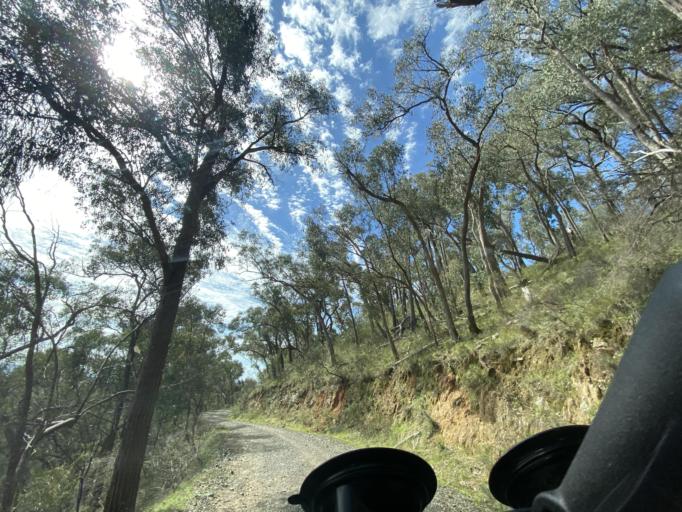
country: AU
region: Victoria
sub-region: Mansfield
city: Mansfield
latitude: -36.8097
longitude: 146.1031
